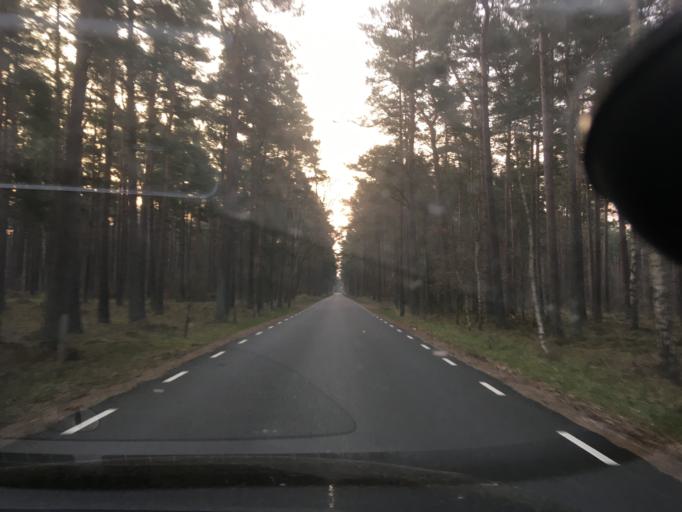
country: SE
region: Skane
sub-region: Simrishamns Kommun
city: Simrishamn
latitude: 55.3932
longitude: 14.1816
